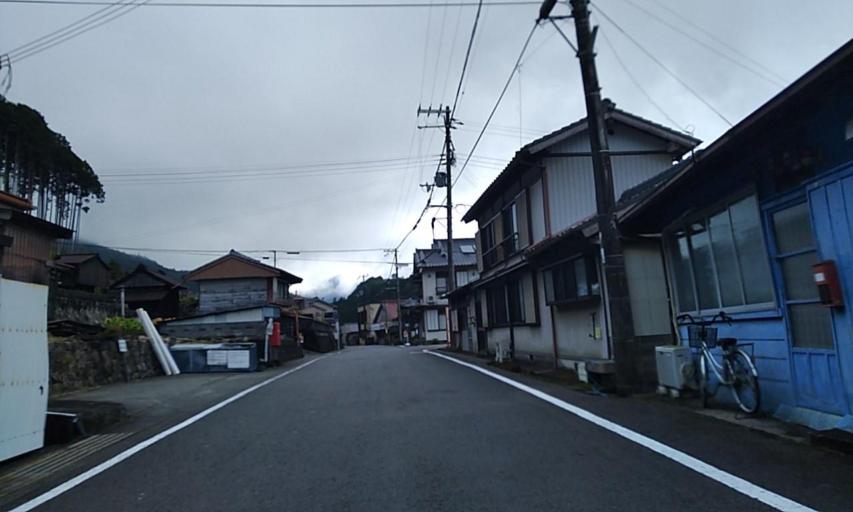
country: JP
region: Wakayama
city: Shingu
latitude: 33.9309
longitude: 135.9656
